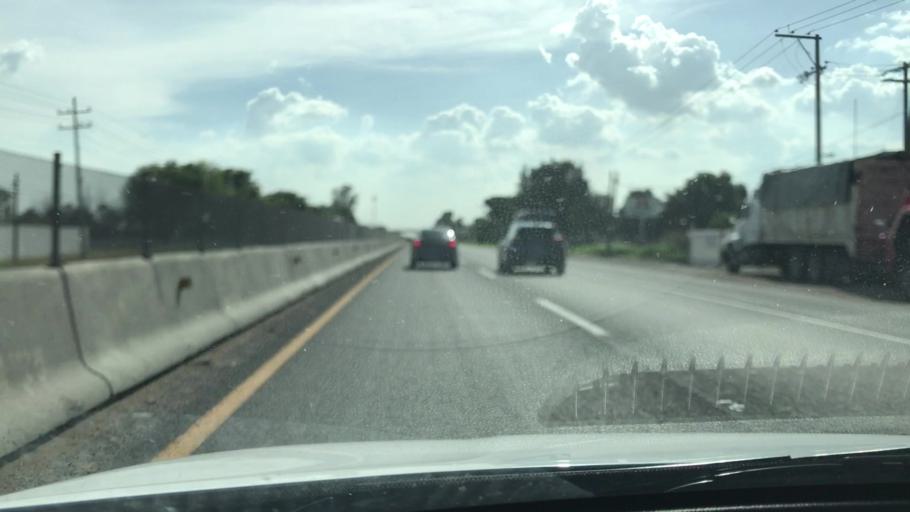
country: MX
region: Guanajuato
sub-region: Cortazar
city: Colonia la Calzada (La Olla)
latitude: 20.5105
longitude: -100.9635
